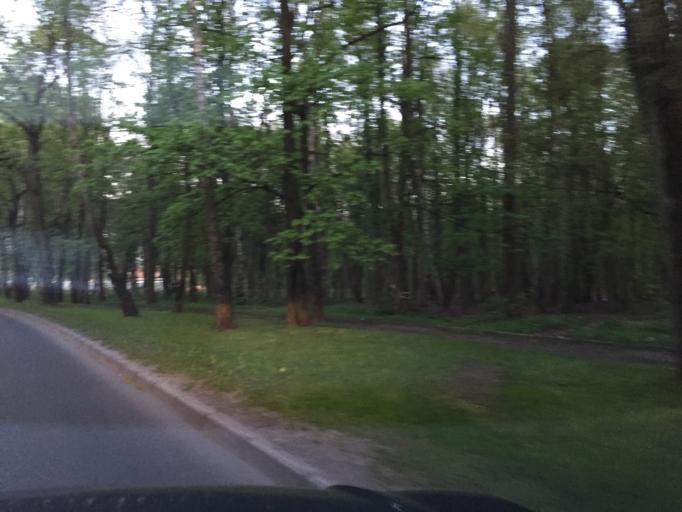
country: RU
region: Kaliningrad
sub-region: Gorod Kaliningrad
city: Kaliningrad
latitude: 54.7151
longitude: 20.4809
